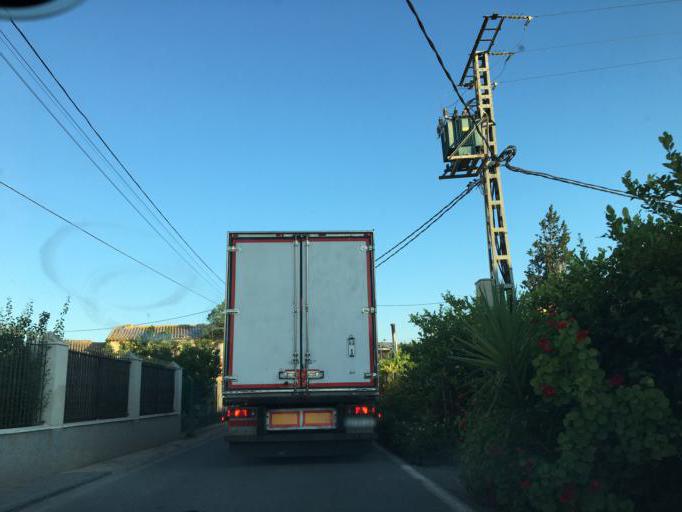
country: ES
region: Murcia
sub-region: Murcia
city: Santomera
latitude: 38.0129
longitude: -1.0562
